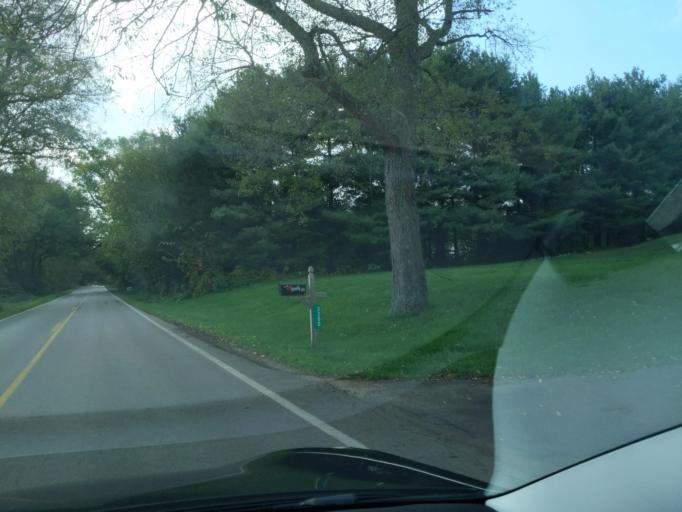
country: US
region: Michigan
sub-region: Ingham County
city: Leslie
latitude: 42.3713
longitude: -84.4461
